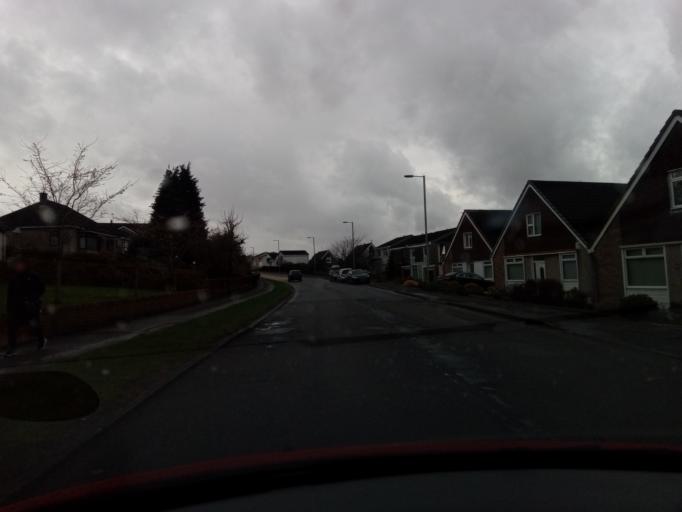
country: GB
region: Scotland
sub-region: East Dunbartonshire
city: Kirkintilloch
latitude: 55.9256
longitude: -4.1690
